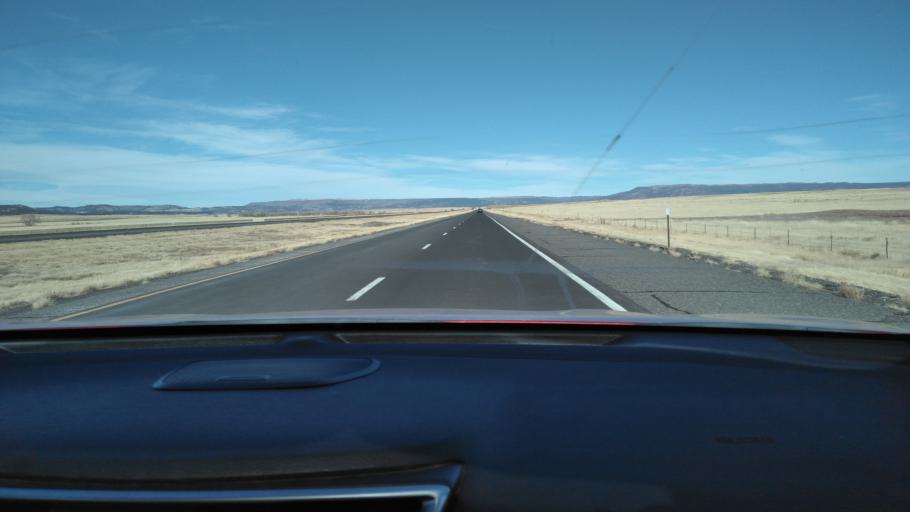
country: US
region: New Mexico
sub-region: Colfax County
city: Raton
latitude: 36.7337
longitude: -104.4571
